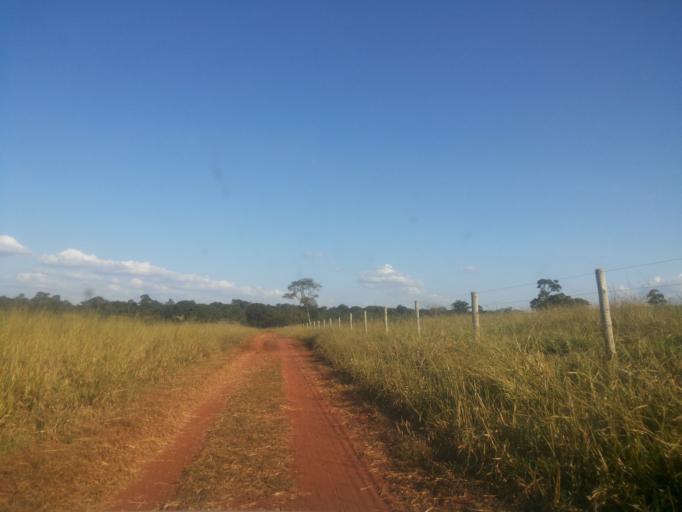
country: BR
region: Minas Gerais
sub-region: Santa Vitoria
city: Santa Vitoria
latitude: -19.0072
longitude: -50.4540
